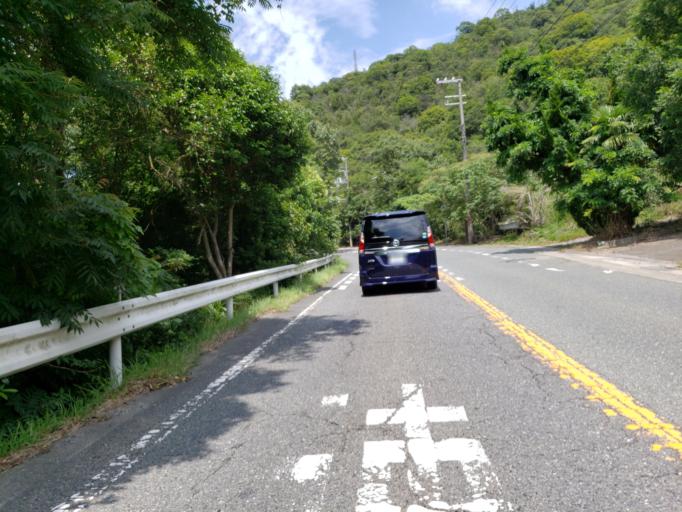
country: JP
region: Hyogo
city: Aioi
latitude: 34.7796
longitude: 134.4357
